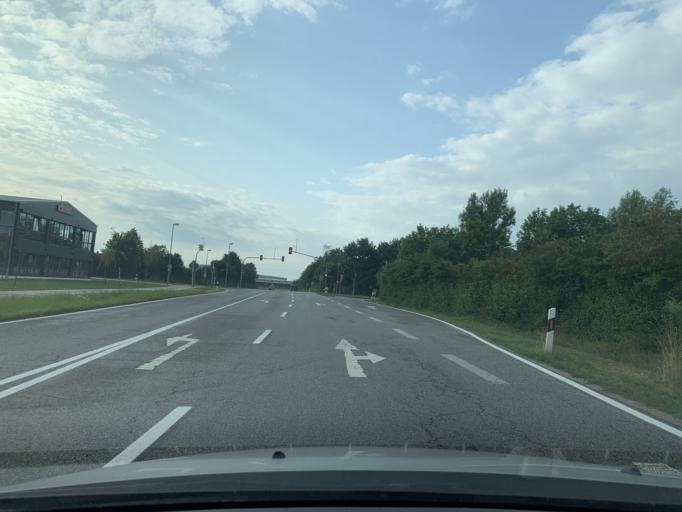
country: DE
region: Bavaria
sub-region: Upper Bavaria
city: Muehldorf
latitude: 48.2613
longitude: 12.5432
